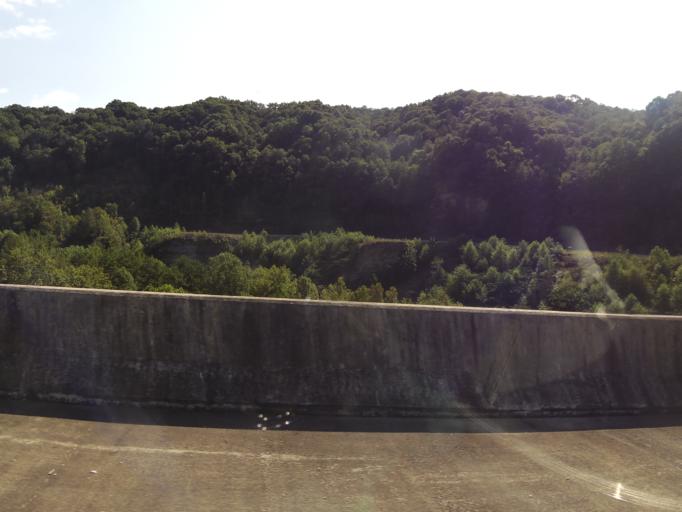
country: US
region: Kentucky
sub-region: Bell County
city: Pineville
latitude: 36.7442
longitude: -83.6097
